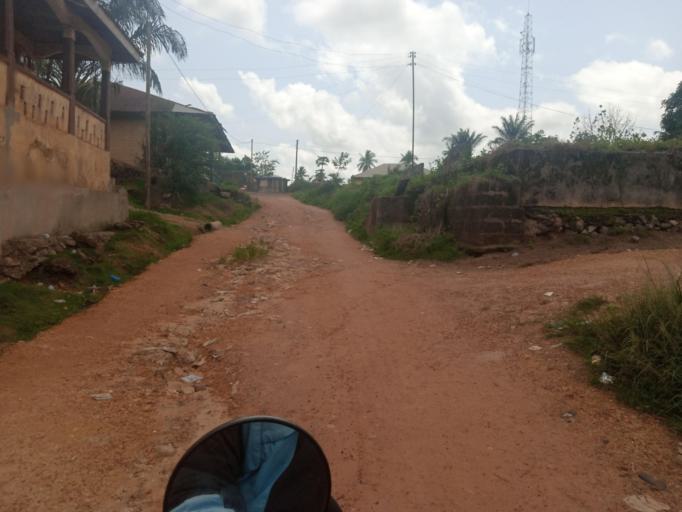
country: SL
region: Southern Province
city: Bo
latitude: 7.9553
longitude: -11.7398
